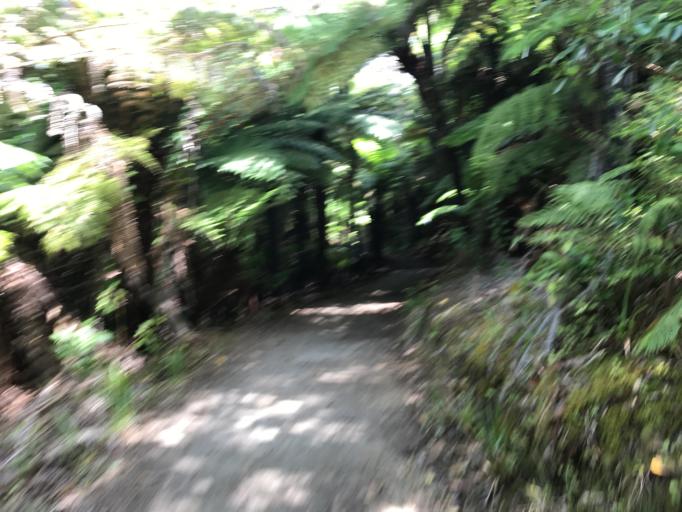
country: NZ
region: Marlborough
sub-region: Marlborough District
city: Picton
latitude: -41.2564
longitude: 173.9379
